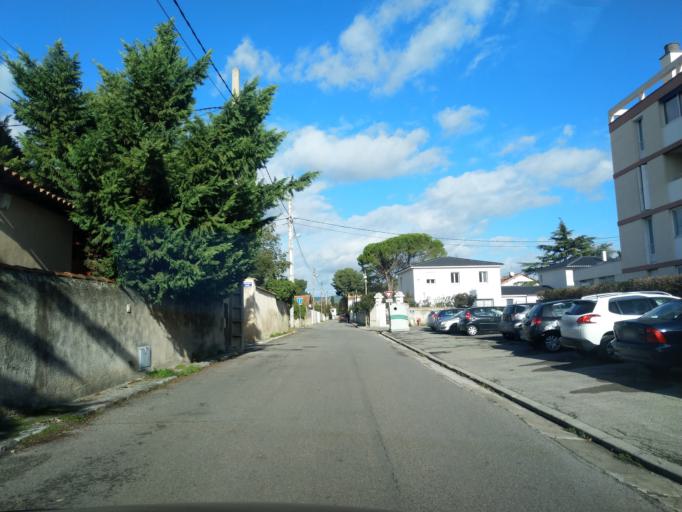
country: FR
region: Provence-Alpes-Cote d'Azur
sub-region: Departement des Bouches-du-Rhone
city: Marseille 12
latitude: 43.3108
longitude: 5.4351
